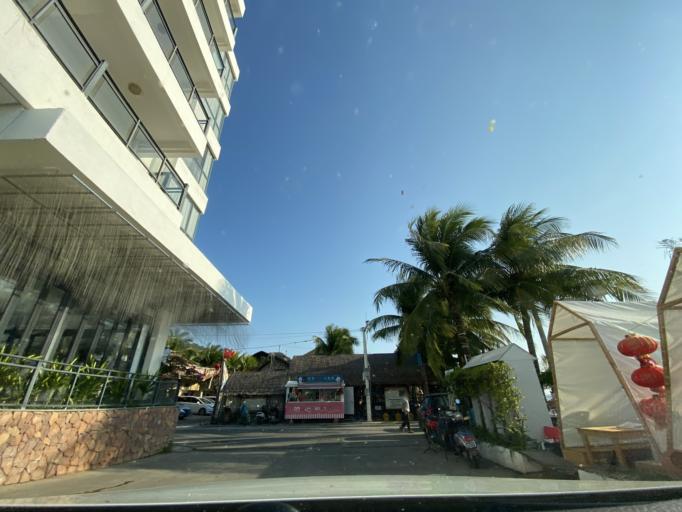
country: CN
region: Hainan
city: Yingzhou
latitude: 18.3873
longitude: 109.8180
